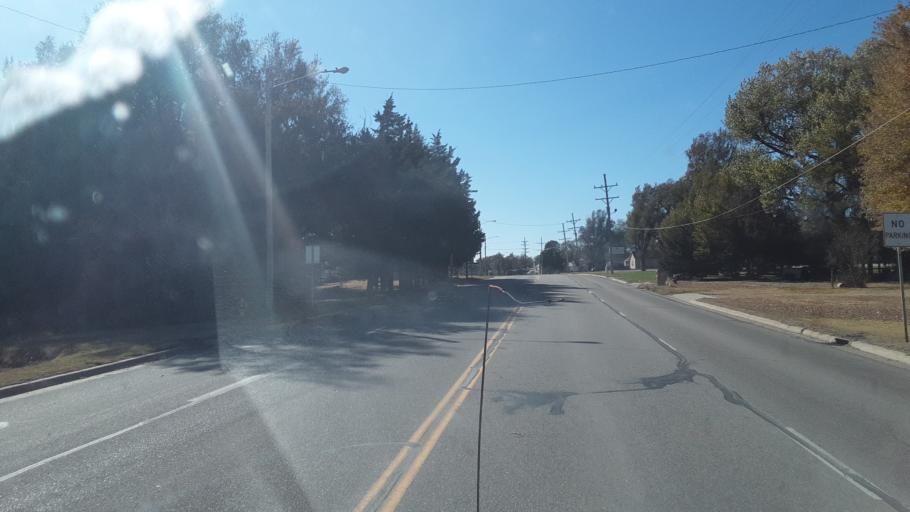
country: US
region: Kansas
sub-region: Rice County
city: Lyons
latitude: 38.3512
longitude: -98.1861
